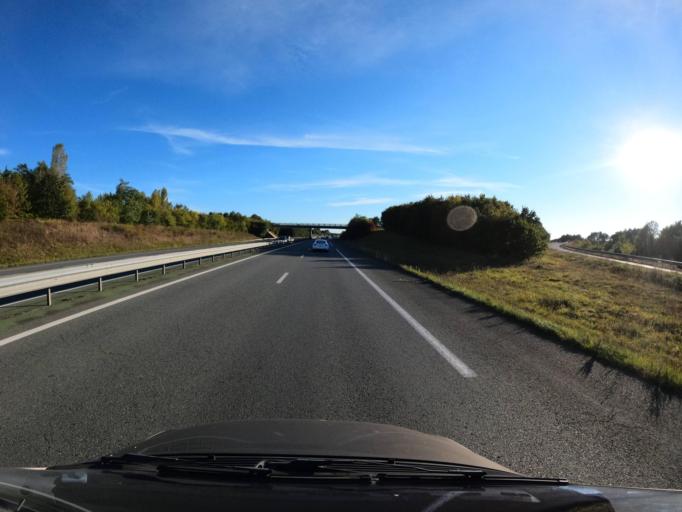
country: FR
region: Pays de la Loire
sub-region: Departement de Maine-et-Loire
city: Nuaille
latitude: 47.0878
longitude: -0.8240
